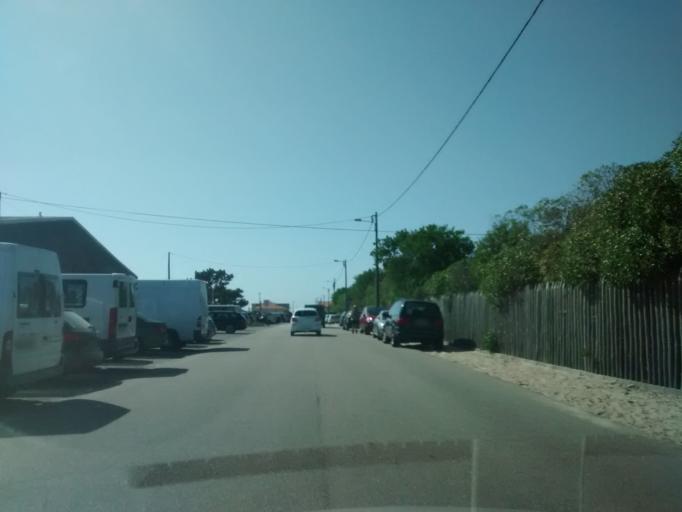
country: PT
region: Aveiro
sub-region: Ilhavo
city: Gafanha da Nazare
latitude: 40.6669
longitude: -8.7381
